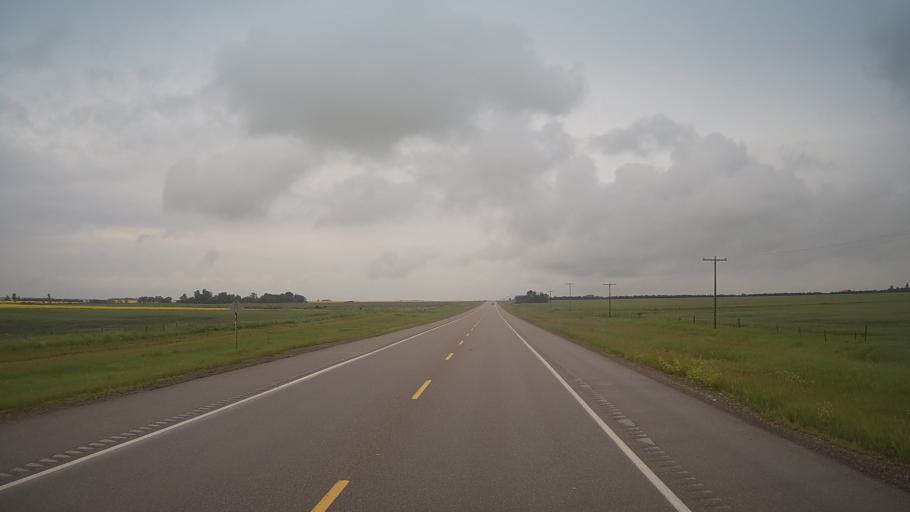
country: CA
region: Saskatchewan
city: Unity
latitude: 52.4349
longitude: -108.9379
